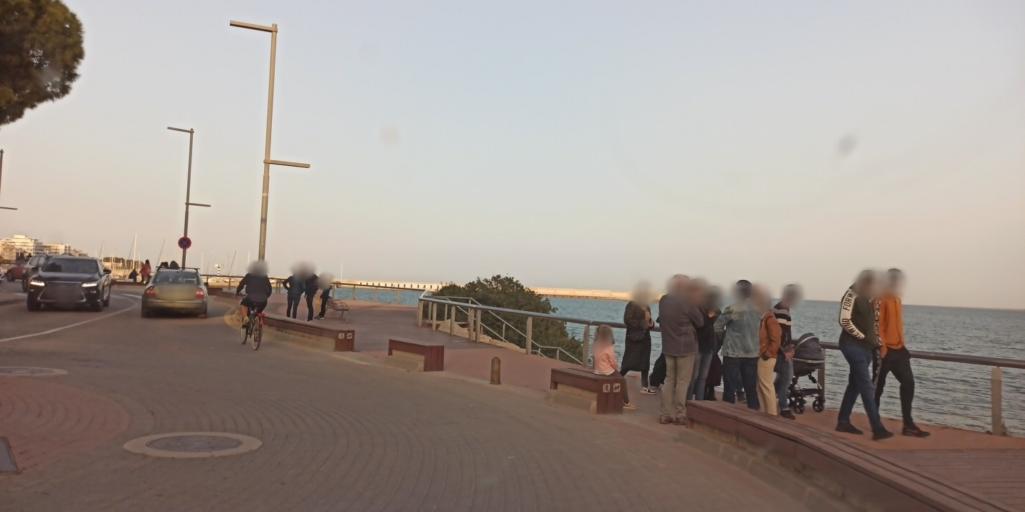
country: ES
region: Catalonia
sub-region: Provincia de Tarragona
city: L'Ampolla
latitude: 40.8085
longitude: 0.7048
